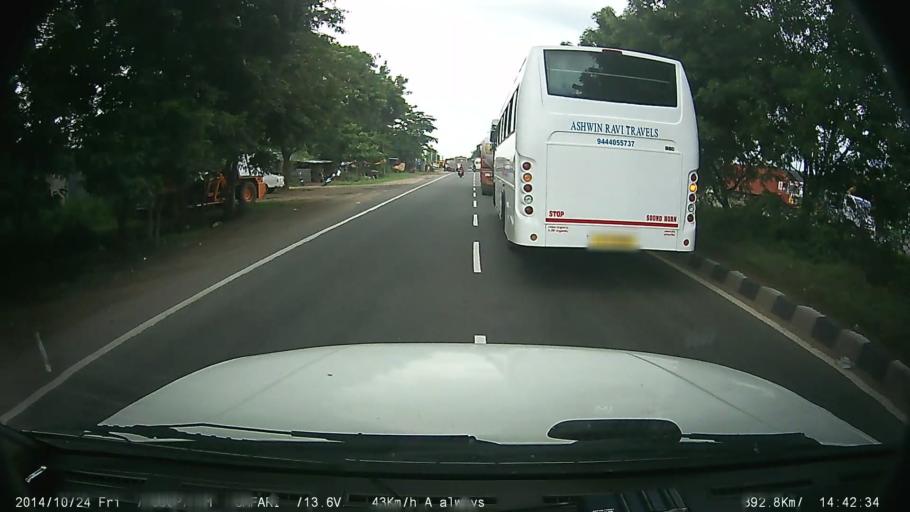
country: IN
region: Tamil Nadu
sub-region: Kancheepuram
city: Singapperumalkovil
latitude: 12.7695
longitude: 80.0069
